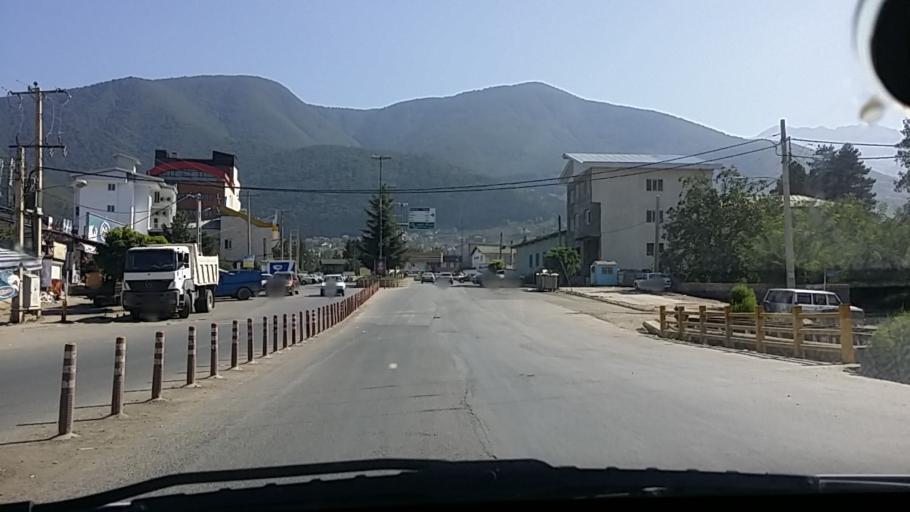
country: IR
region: Mazandaran
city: `Abbasabad
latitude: 36.5071
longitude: 51.1585
